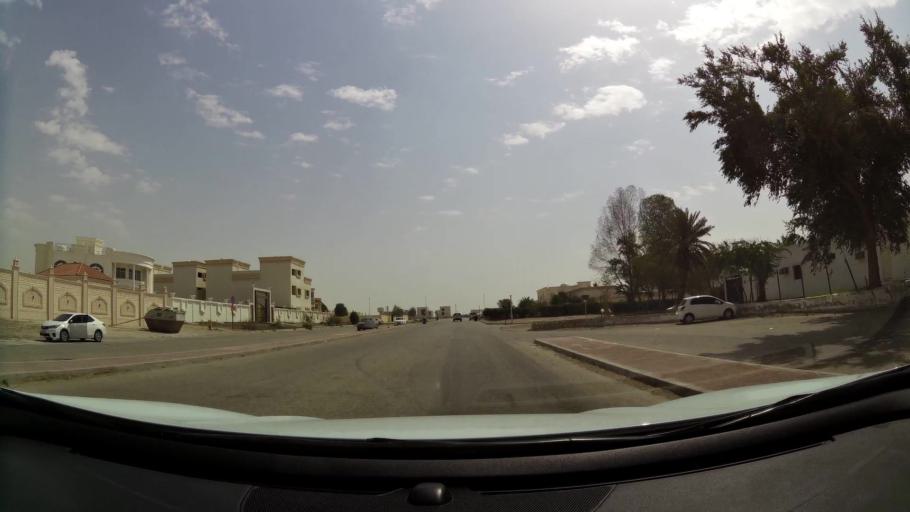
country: AE
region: Abu Dhabi
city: Abu Dhabi
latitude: 24.2999
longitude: 54.6297
